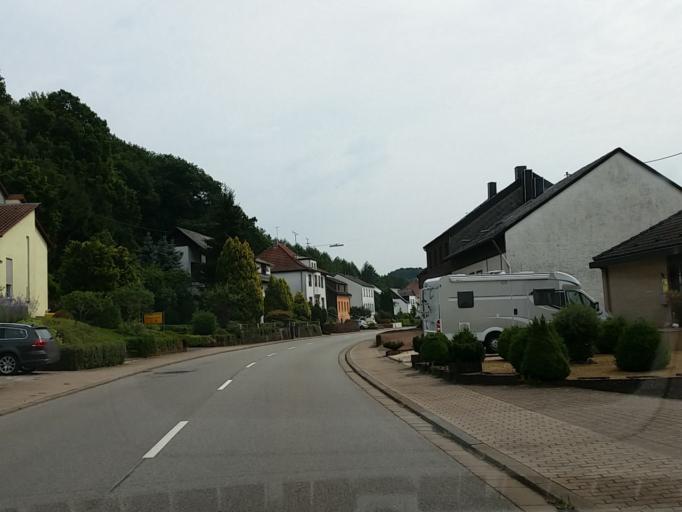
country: DE
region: Saarland
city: Schmelz
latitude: 49.4919
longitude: 6.8413
